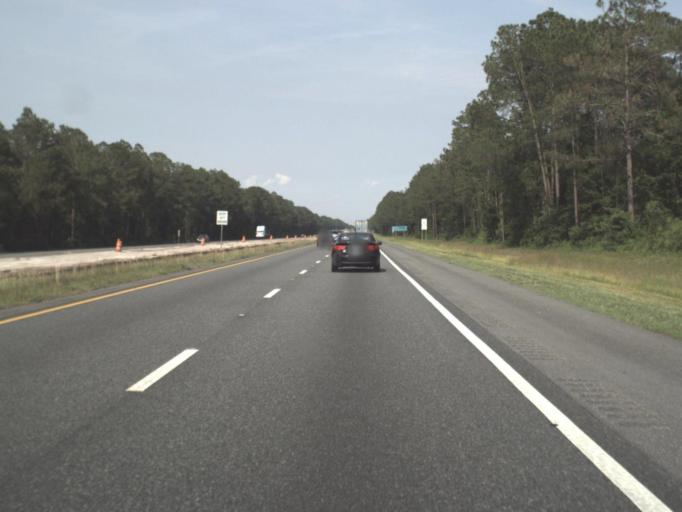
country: US
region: Florida
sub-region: Baker County
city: Macclenny
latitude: 30.2662
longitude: -82.0964
